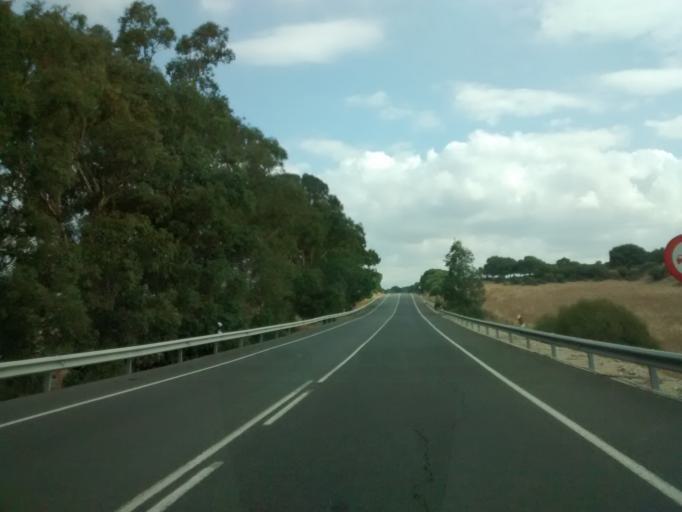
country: ES
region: Andalusia
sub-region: Provincia de Cadiz
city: Barbate de Franco
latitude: 36.2221
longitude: -5.8518
